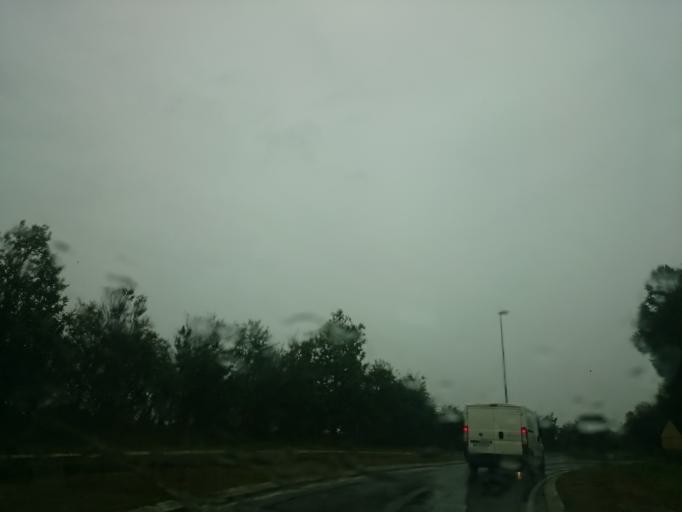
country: FR
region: Brittany
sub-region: Departement du Finistere
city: Gouesnou
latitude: 48.4642
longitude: -4.4493
